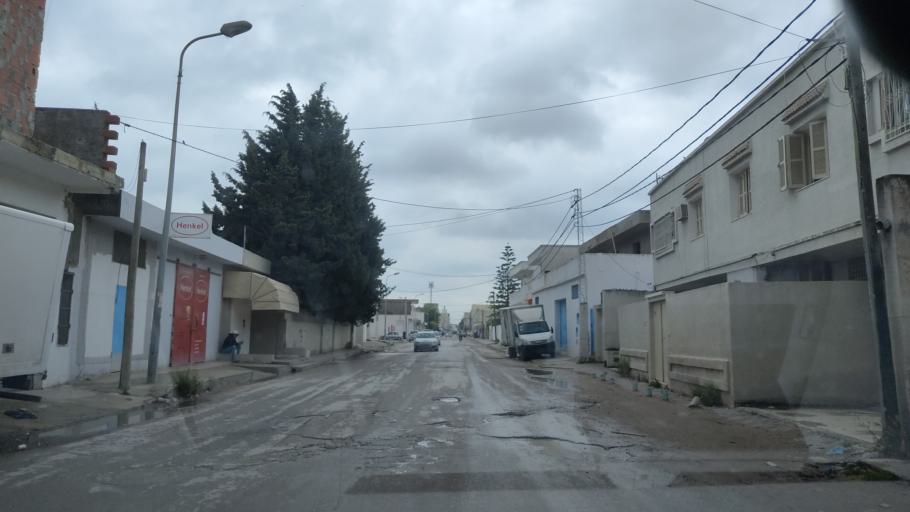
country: TN
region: Ariana
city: Ariana
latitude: 36.8769
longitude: 10.2172
